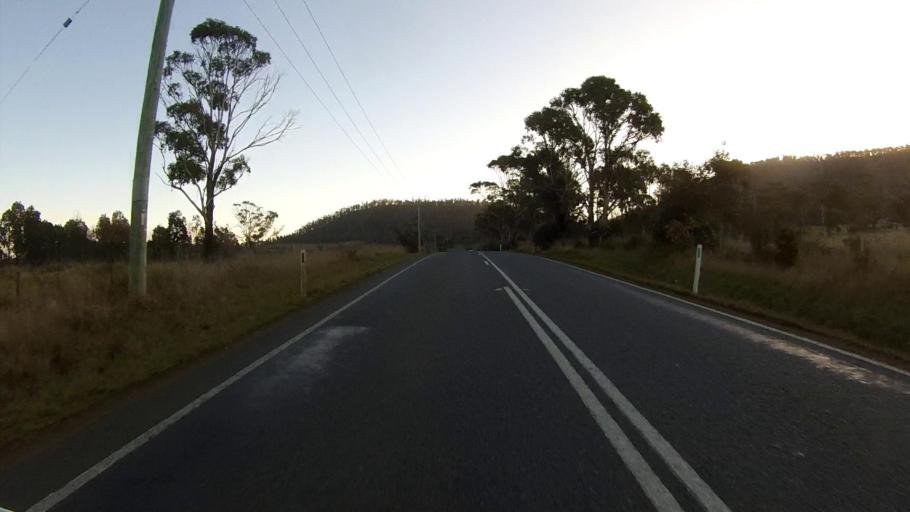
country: AU
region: Tasmania
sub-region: Sorell
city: Sorell
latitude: -42.8166
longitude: 147.7596
